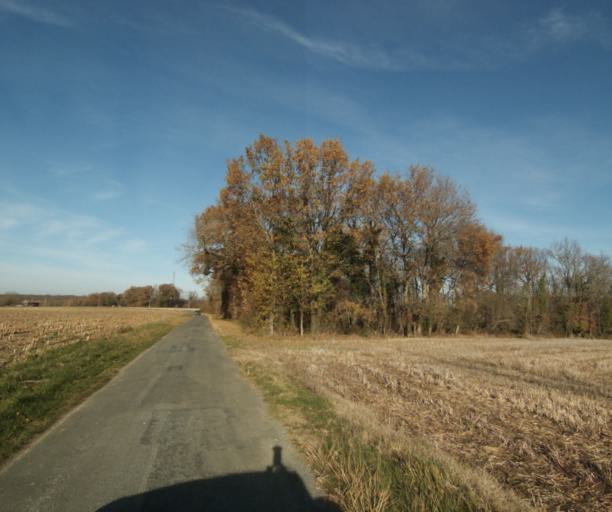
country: FR
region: Poitou-Charentes
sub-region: Departement de la Charente-Maritime
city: Ecoyeux
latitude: 45.7561
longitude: -0.4940
